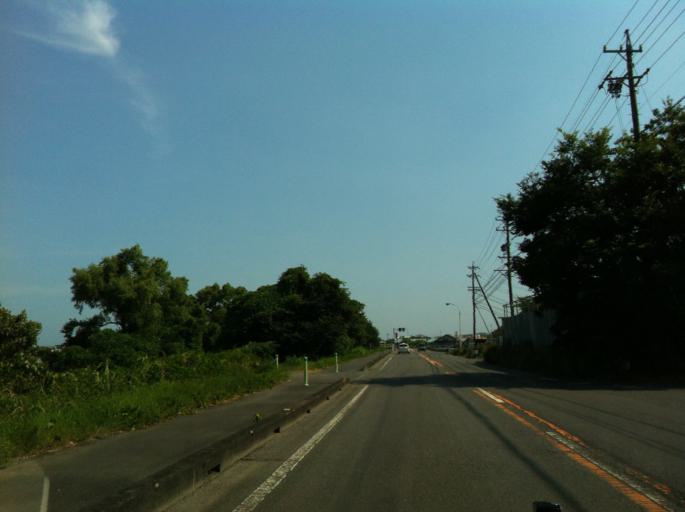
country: JP
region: Shizuoka
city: Shizuoka-shi
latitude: 35.0004
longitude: 138.3539
